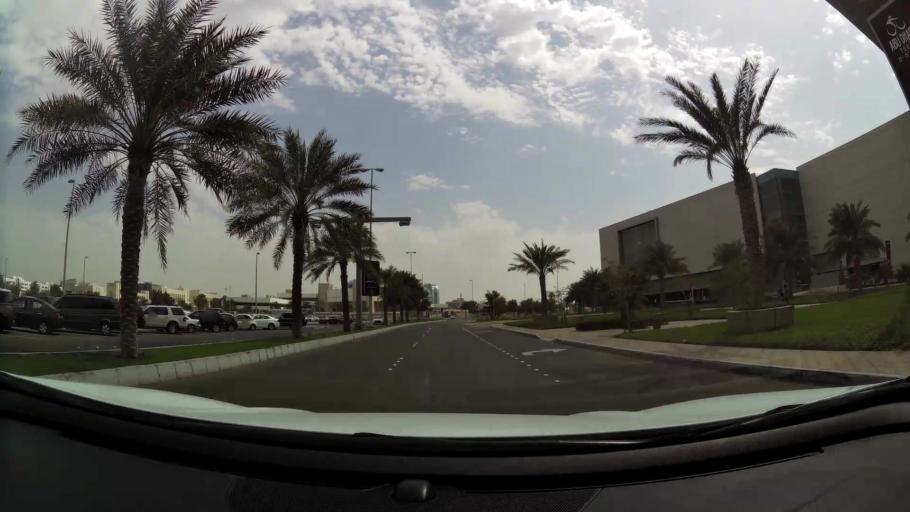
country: AE
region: Abu Dhabi
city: Abu Dhabi
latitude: 24.4652
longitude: 54.3295
